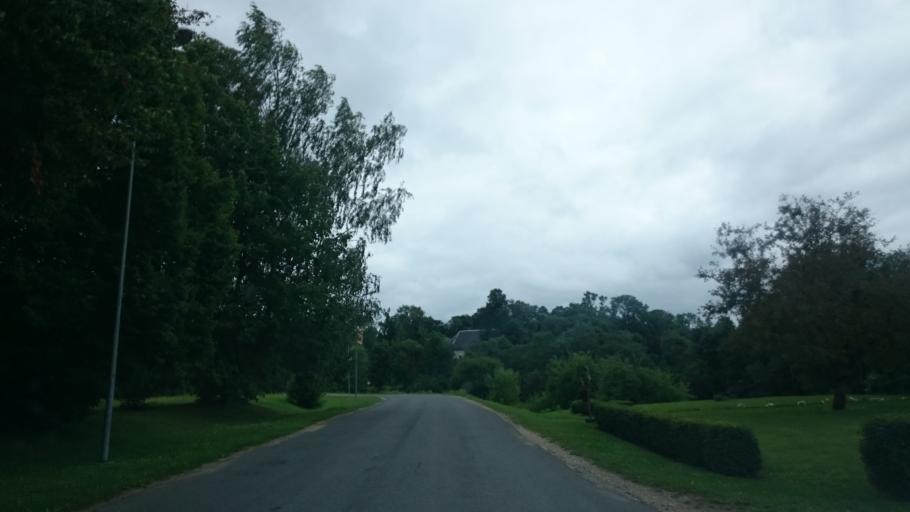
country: LV
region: Durbe
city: Liegi
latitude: 56.7382
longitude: 21.3821
